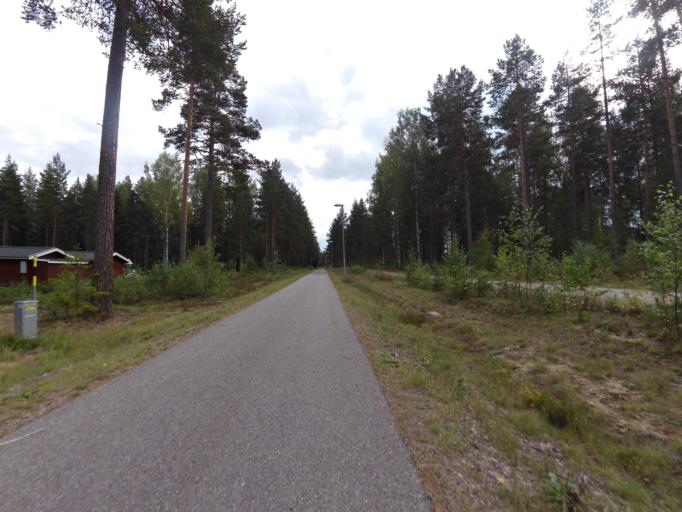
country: SE
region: Gaevleborg
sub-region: Sandvikens Kommun
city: Sandviken
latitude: 60.6830
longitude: 16.8163
